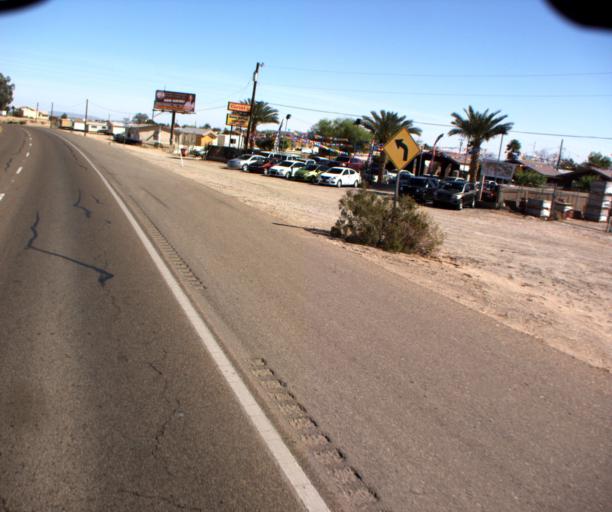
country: US
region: Arizona
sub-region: Yuma County
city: Somerton
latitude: 32.6125
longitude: -114.6501
